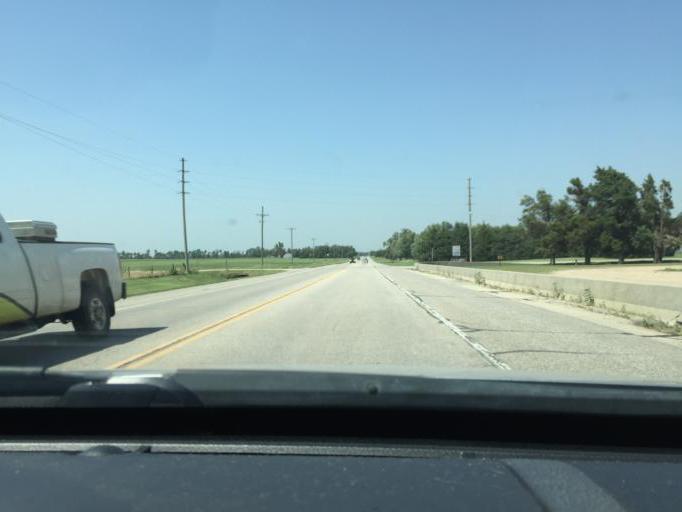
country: US
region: Kansas
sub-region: Reno County
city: Haven
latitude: 37.9546
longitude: -97.8668
